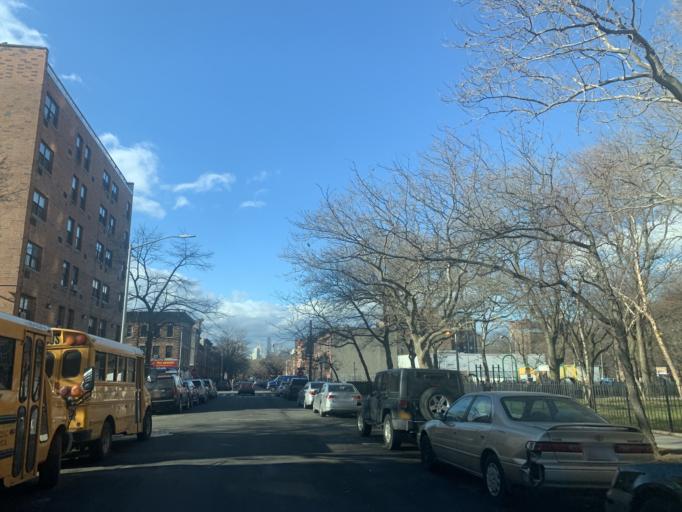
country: US
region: New York
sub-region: Kings County
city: Brooklyn
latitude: 40.6957
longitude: -73.9397
